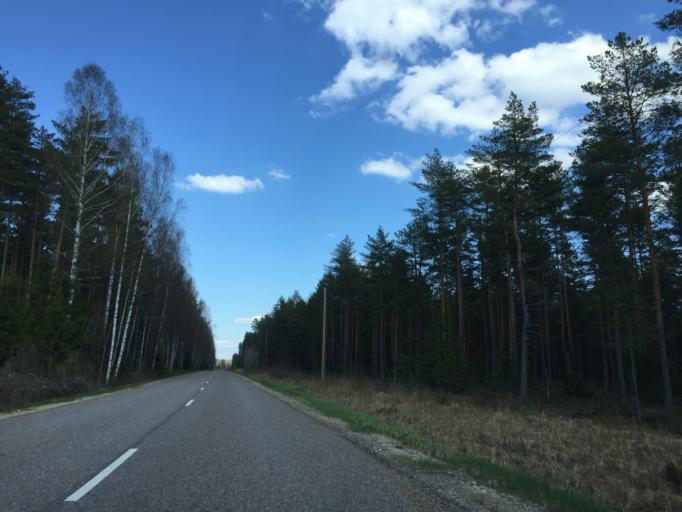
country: LV
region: Saulkrastu
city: Saulkrasti
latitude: 57.2428
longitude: 24.4865
